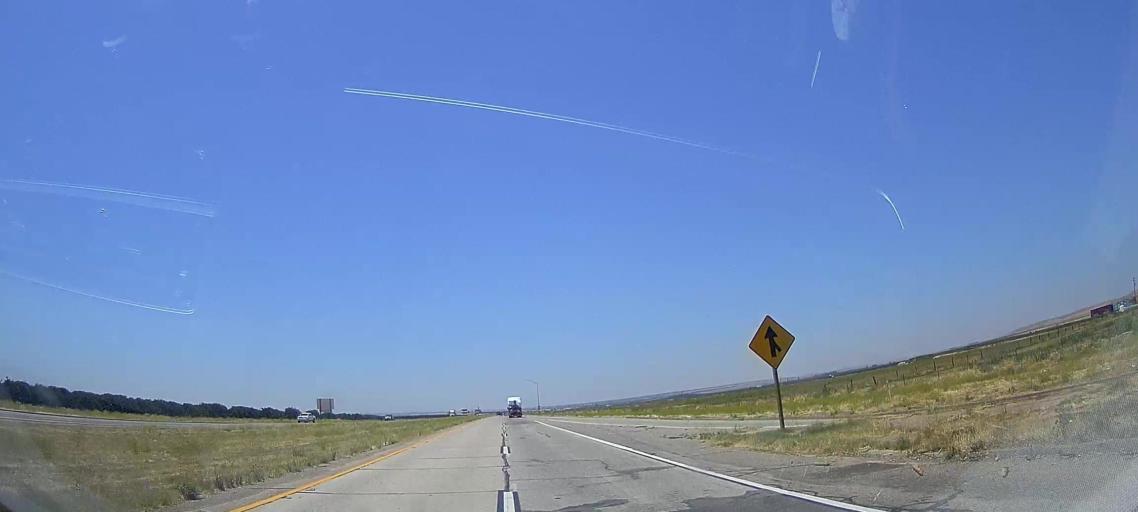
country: US
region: California
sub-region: Kern County
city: Arvin
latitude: 35.3305
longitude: -118.8102
